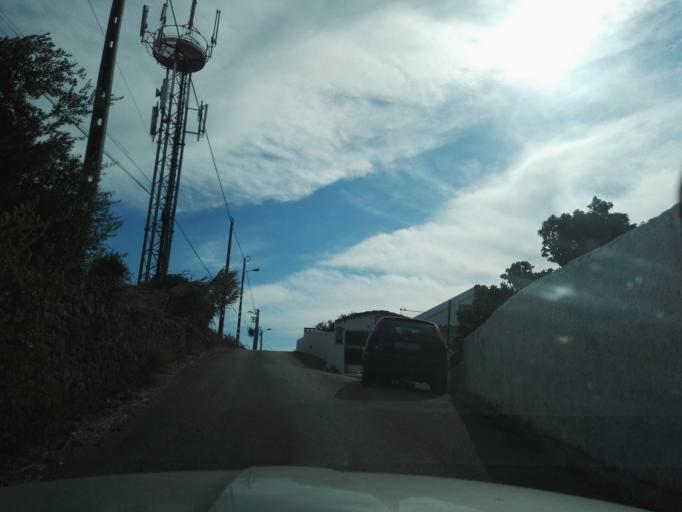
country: PT
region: Lisbon
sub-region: Vila Franca de Xira
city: Sao Joao dos Montes
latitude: 38.9601
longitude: -9.0245
